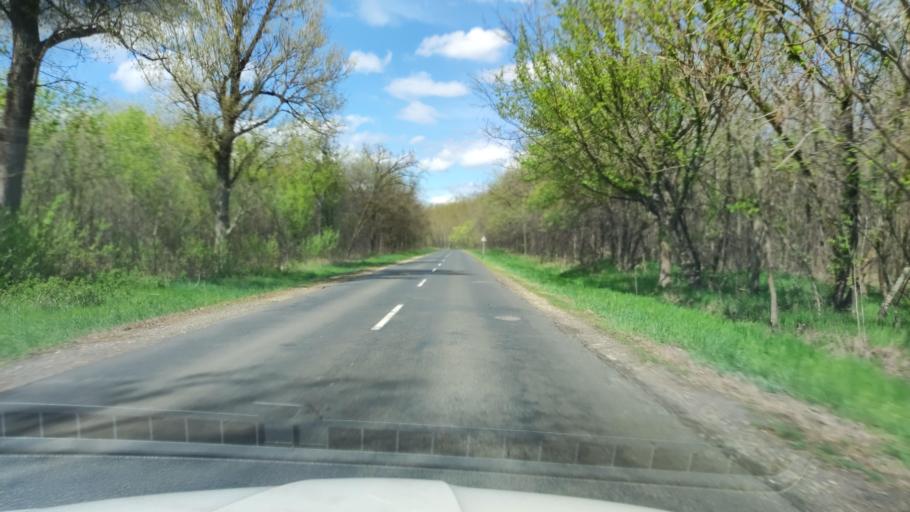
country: HU
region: Pest
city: Cegled
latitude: 47.1505
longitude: 19.8639
